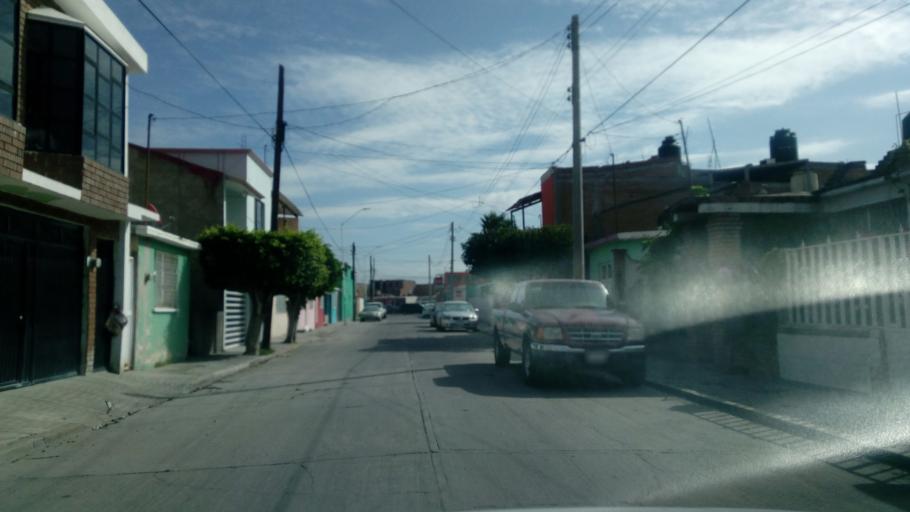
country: MX
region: Durango
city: Victoria de Durango
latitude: 24.0107
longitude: -104.6560
